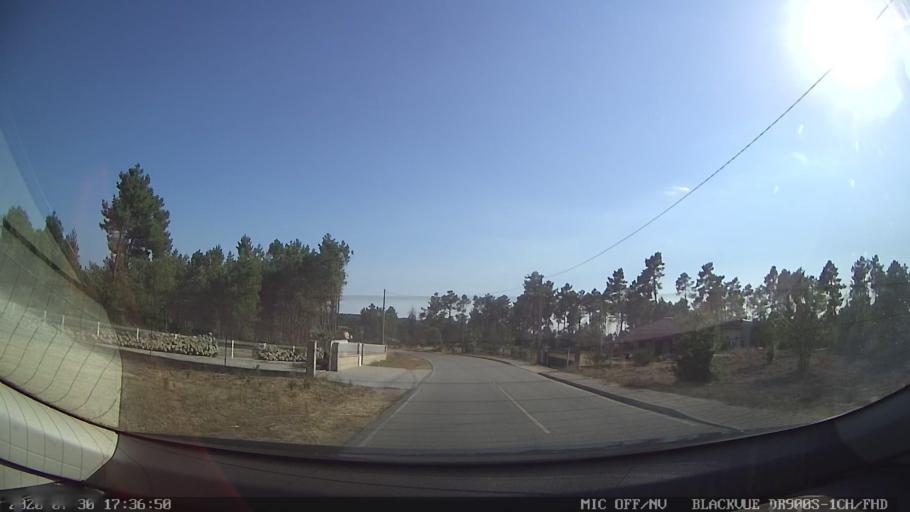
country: PT
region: Vila Real
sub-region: Murca
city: Murca
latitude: 41.3632
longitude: -7.4923
